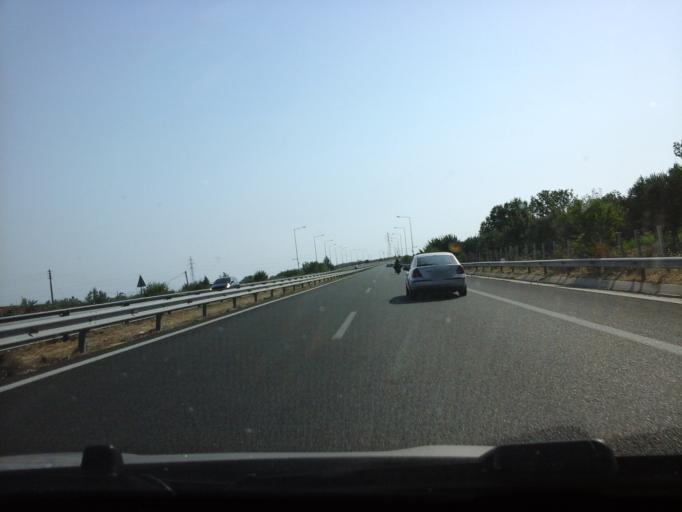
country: GR
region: East Macedonia and Thrace
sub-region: Nomos Evrou
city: Alexandroupoli
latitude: 40.8637
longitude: 25.7626
